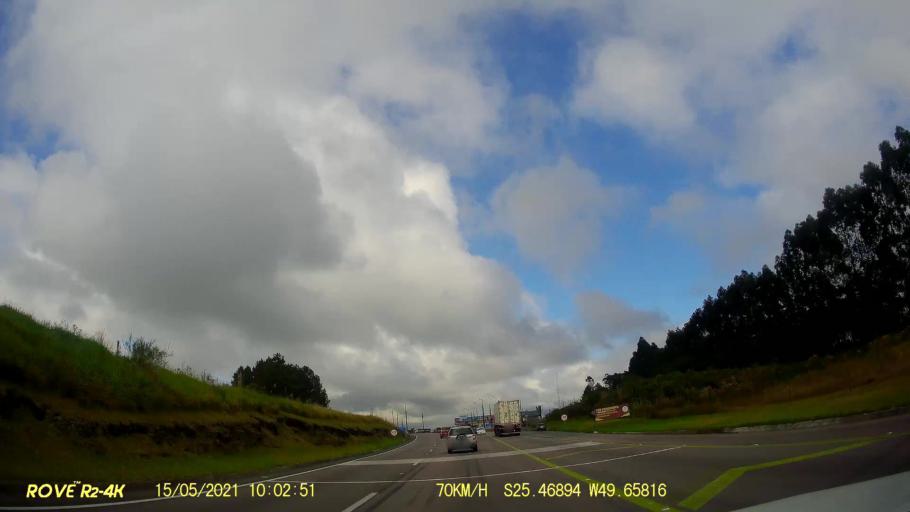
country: BR
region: Parana
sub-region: Campo Largo
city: Campo Largo
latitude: -25.4689
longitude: -49.6582
